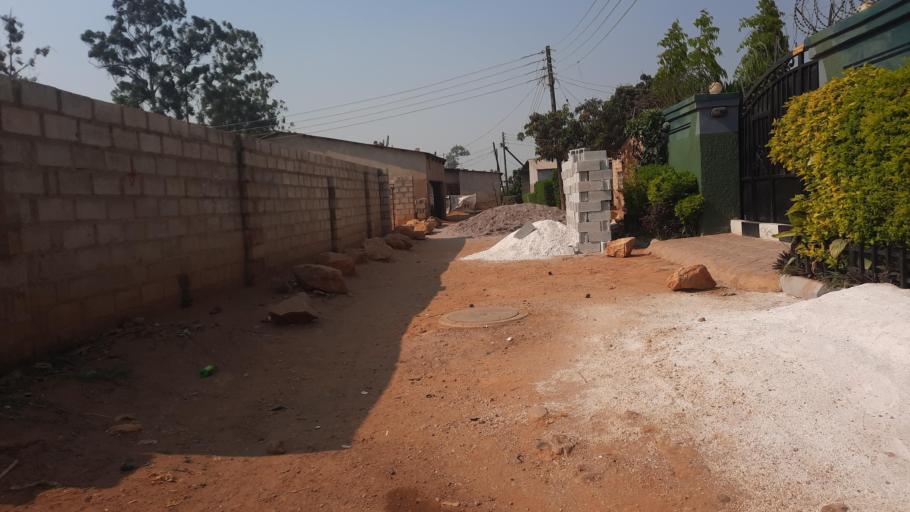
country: ZM
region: Lusaka
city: Lusaka
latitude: -15.3986
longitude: 28.3823
